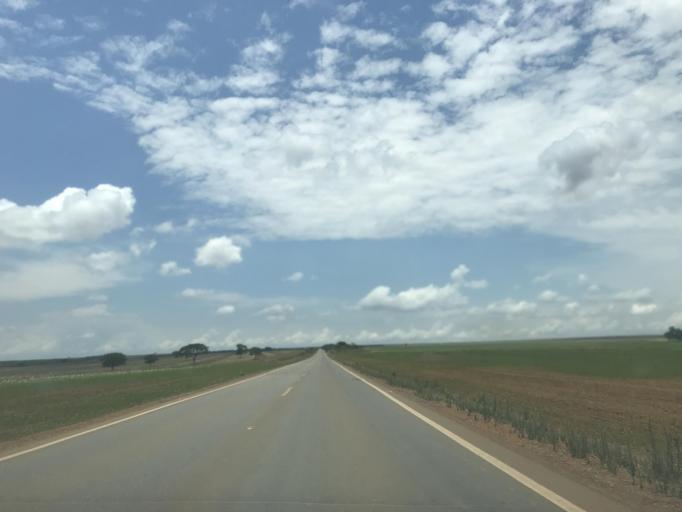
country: BR
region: Goias
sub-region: Luziania
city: Luziania
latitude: -16.5010
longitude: -48.2109
